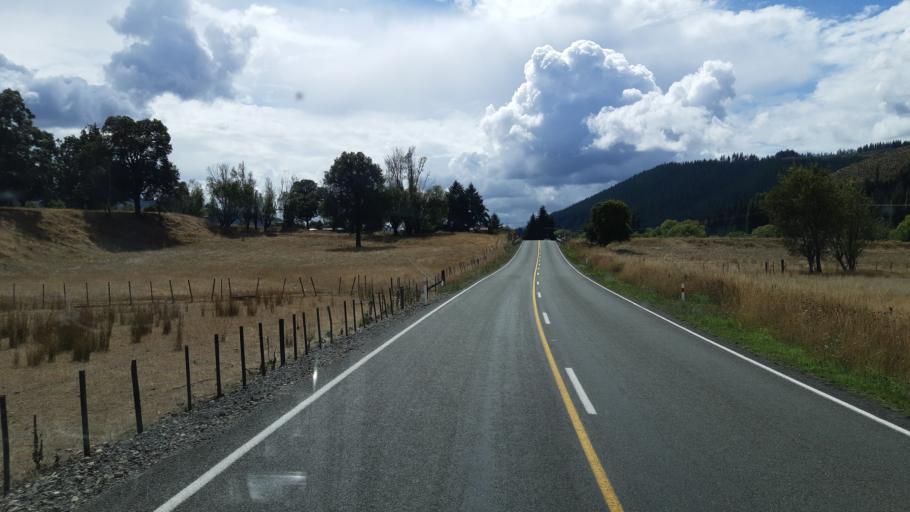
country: NZ
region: Tasman
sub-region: Tasman District
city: Wakefield
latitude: -41.4823
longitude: 172.7999
